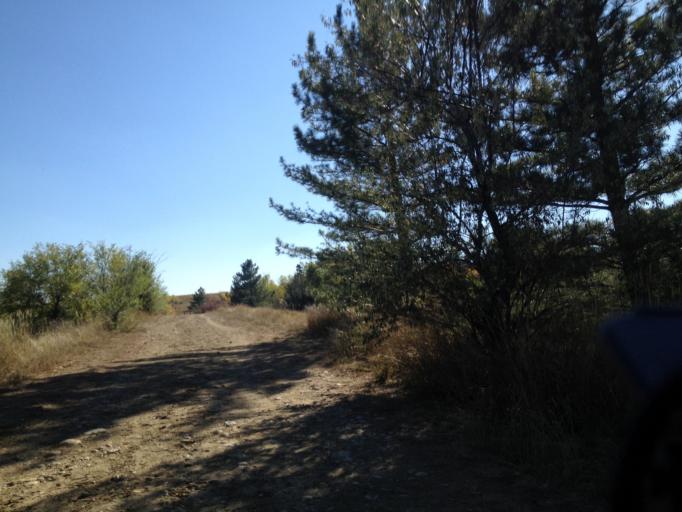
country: US
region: Colorado
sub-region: Boulder County
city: Boulder
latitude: 39.9800
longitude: -105.2353
